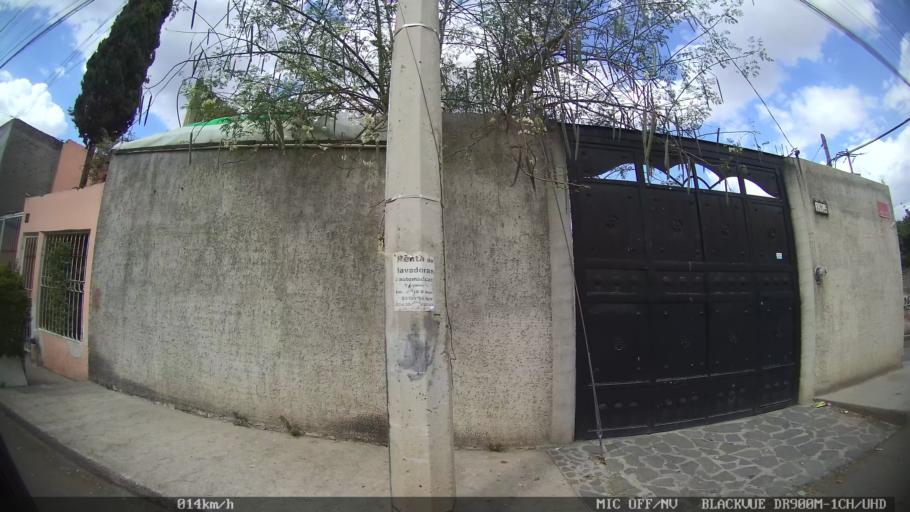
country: MX
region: Jalisco
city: Tlaquepaque
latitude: 20.6625
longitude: -103.2631
